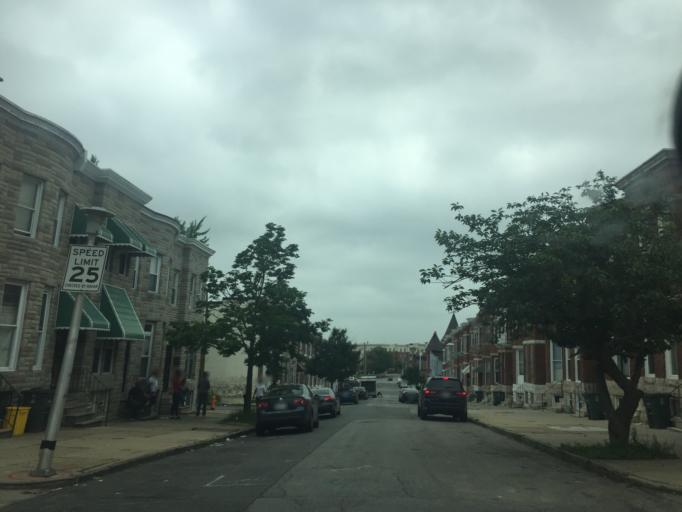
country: US
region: Maryland
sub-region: City of Baltimore
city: Baltimore
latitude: 39.3156
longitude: -76.6470
